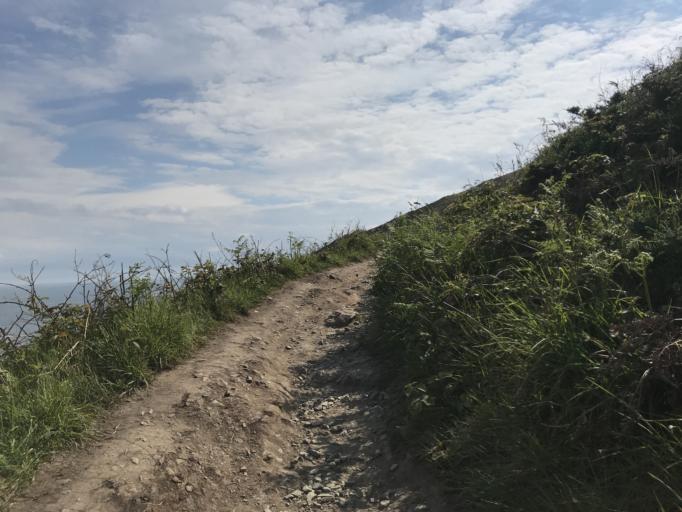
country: IE
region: Leinster
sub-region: Fingal County
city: Howth
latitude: 53.3760
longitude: -6.0465
